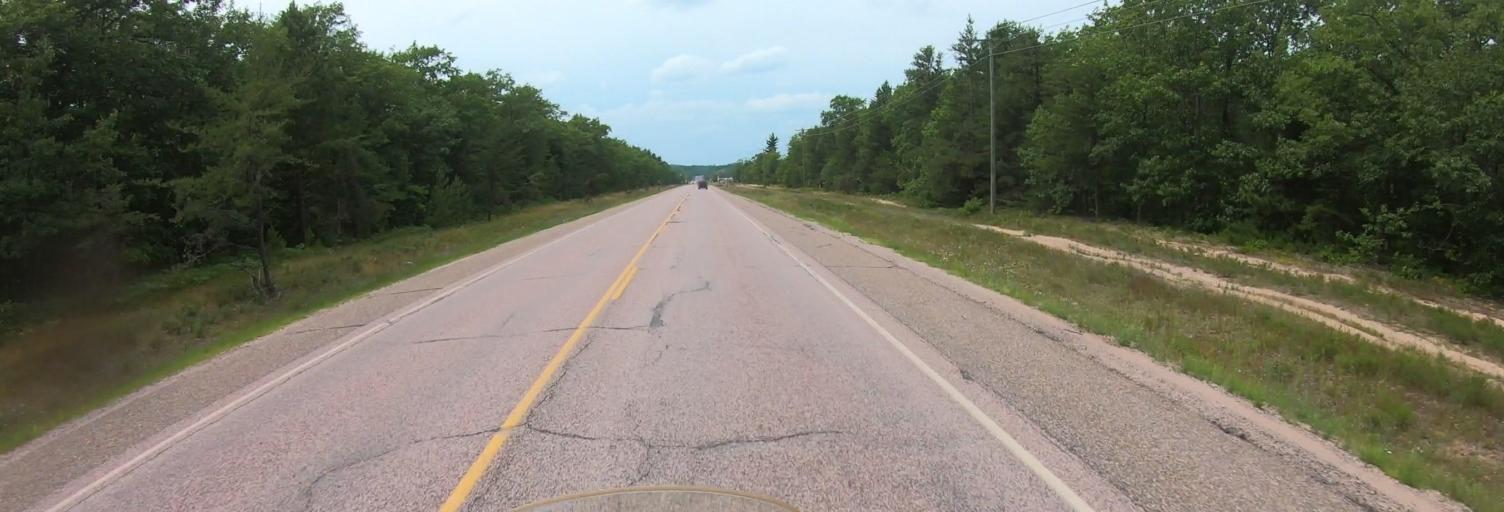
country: US
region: Michigan
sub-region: Marquette County
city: Harvey
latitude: 46.4606
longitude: -87.4161
